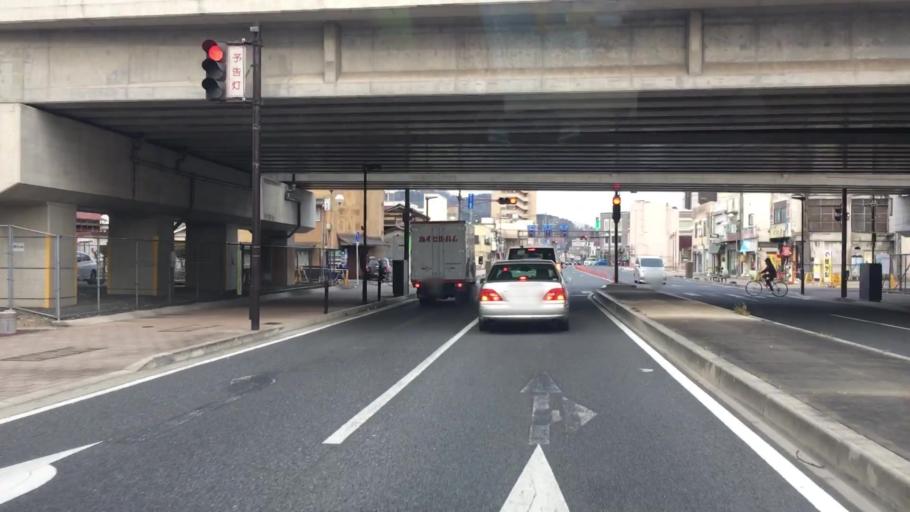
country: JP
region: Gunma
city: Ota
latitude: 36.2941
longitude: 139.3767
